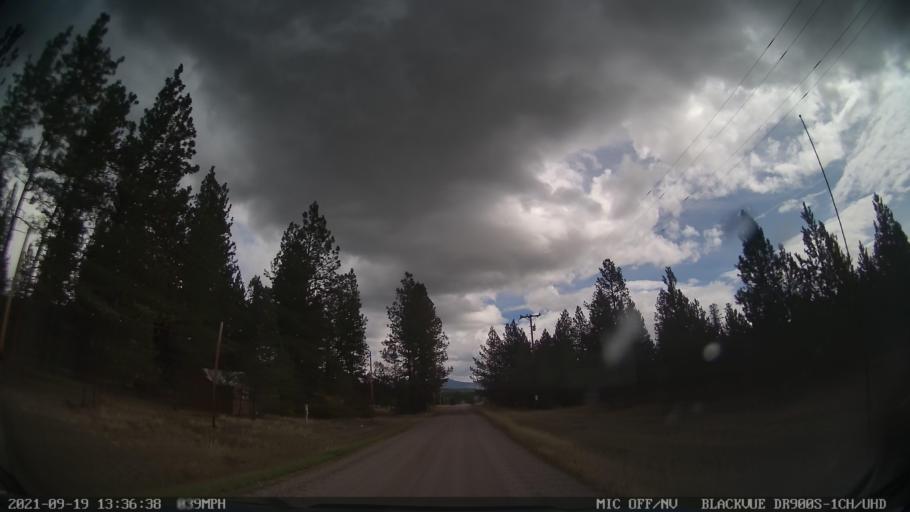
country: US
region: Montana
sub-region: Missoula County
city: Seeley Lake
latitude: 47.1066
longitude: -113.2950
